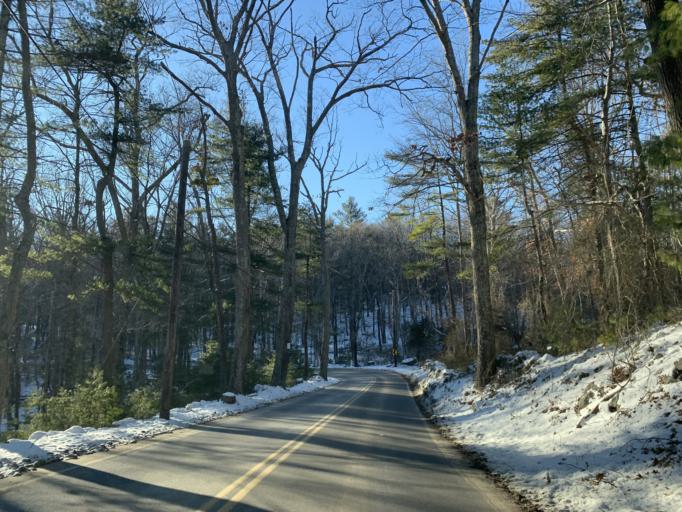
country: US
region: Massachusetts
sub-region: Norfolk County
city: Sharon
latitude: 42.1167
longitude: -71.2074
